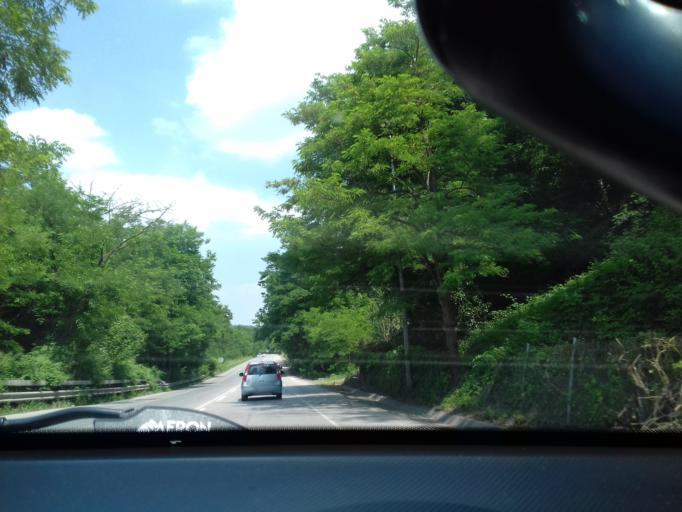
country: TR
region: Sakarya
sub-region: Merkez
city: Sapanca
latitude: 40.6971
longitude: 30.2927
